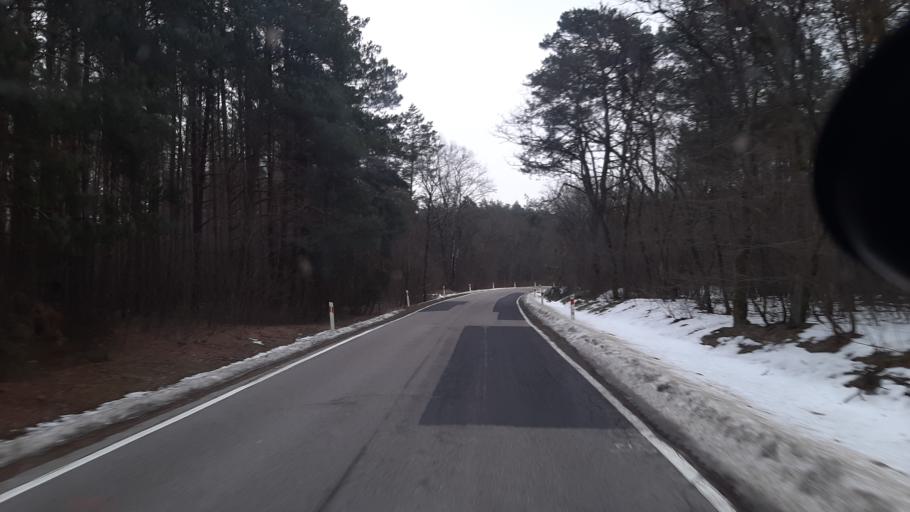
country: PL
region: Lublin Voivodeship
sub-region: Powiat wlodawski
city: Wlodawa
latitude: 51.4904
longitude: 23.6066
